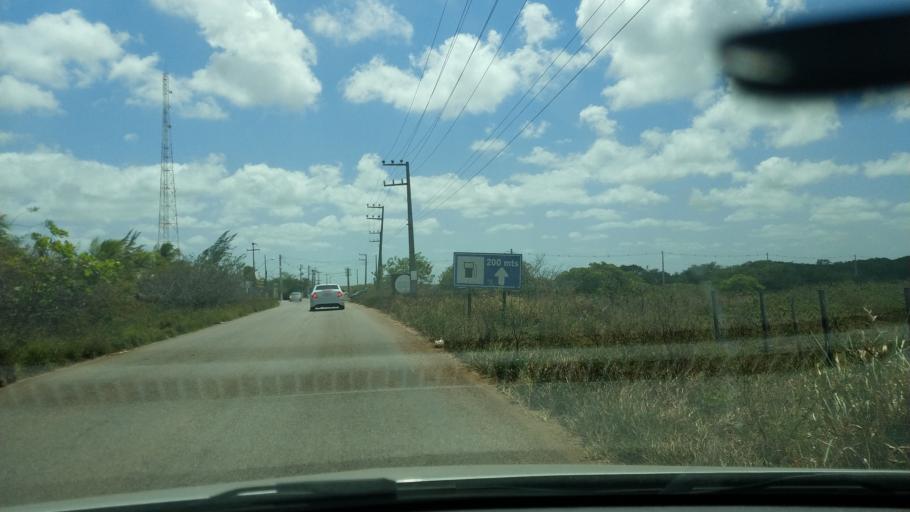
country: BR
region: Rio Grande do Norte
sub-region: Ares
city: Ares
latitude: -6.2324
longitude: -35.0728
